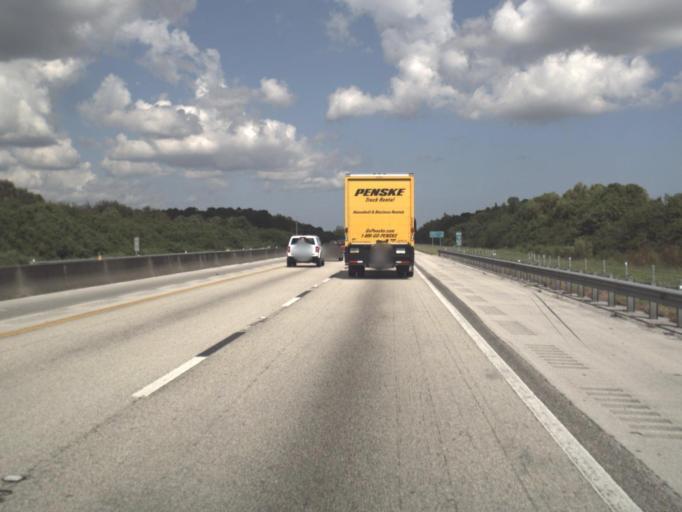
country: US
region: Florida
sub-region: Palm Beach County
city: Palm Beach Gardens
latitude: 26.8507
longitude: -80.1295
